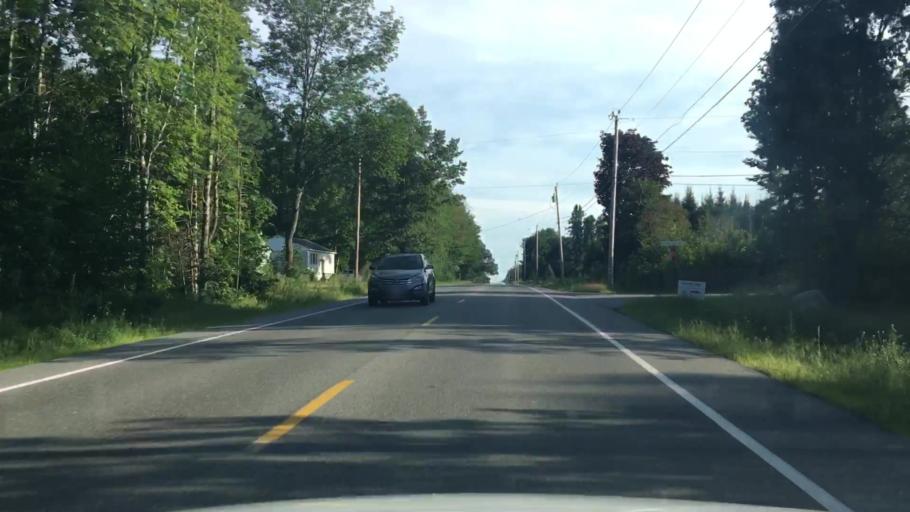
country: US
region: Maine
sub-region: Cumberland County
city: North Windham
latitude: 43.8145
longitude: -70.4413
